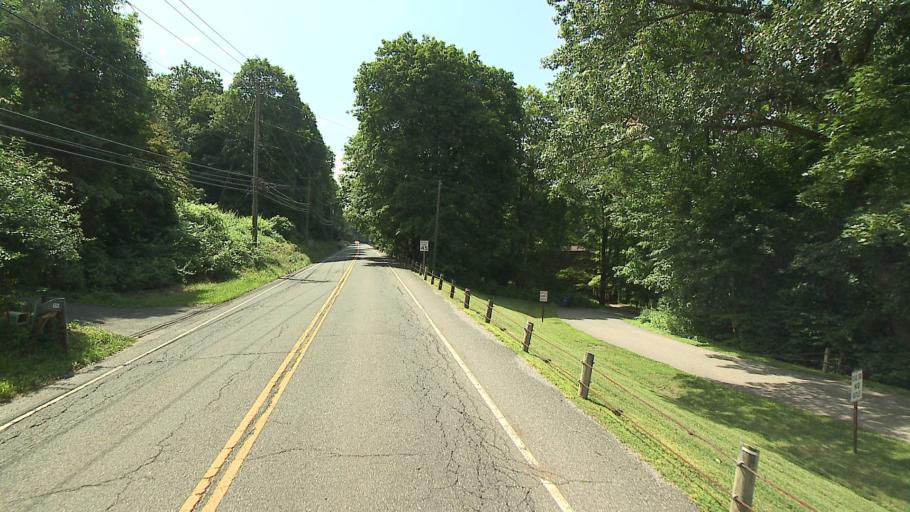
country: US
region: Connecticut
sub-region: Fairfield County
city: Sherman
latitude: 41.5384
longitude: -73.4785
